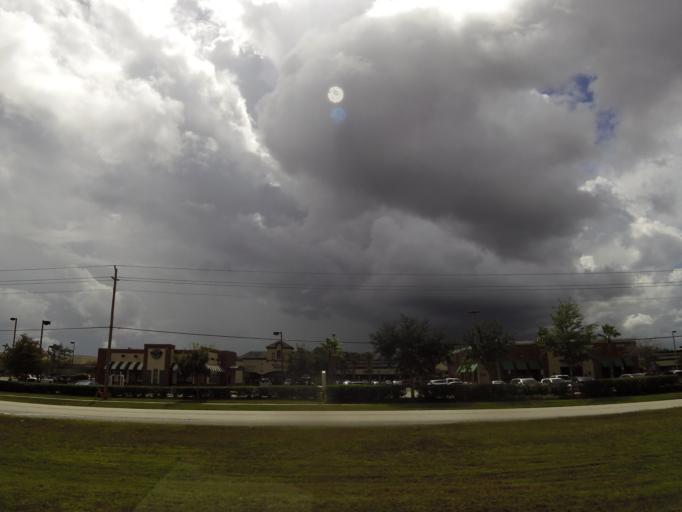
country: US
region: Florida
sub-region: Clay County
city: Lakeside
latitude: 30.1024
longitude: -81.7157
